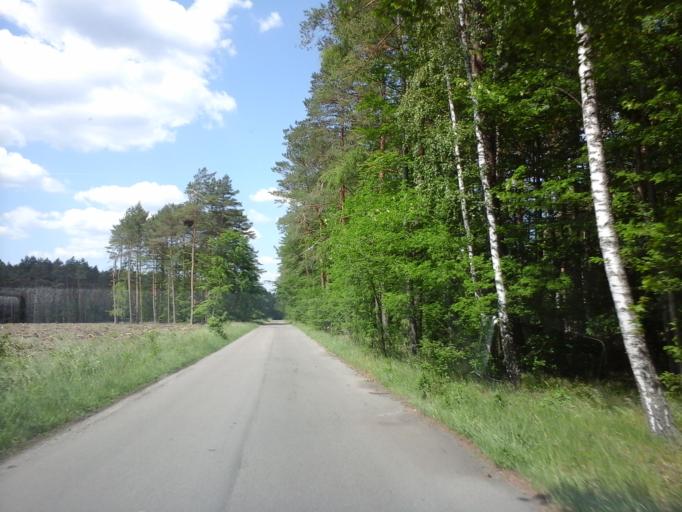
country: PL
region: West Pomeranian Voivodeship
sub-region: Powiat choszczenski
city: Bierzwnik
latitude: 53.0952
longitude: 15.7570
